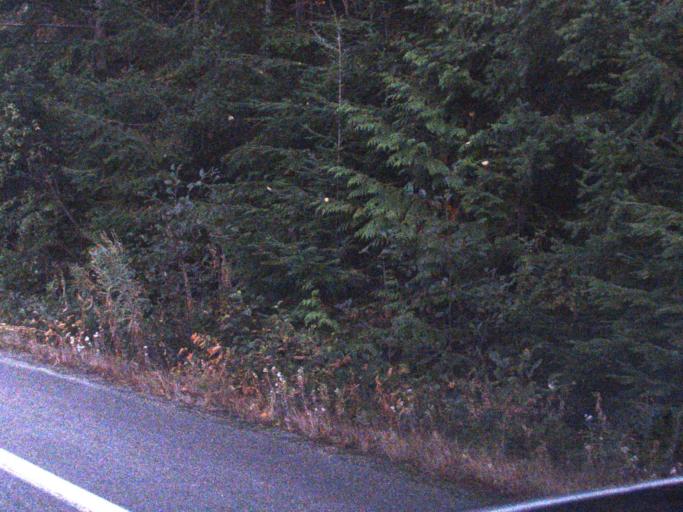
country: US
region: Washington
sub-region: Snohomish County
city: Darrington
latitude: 48.7135
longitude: -120.9957
